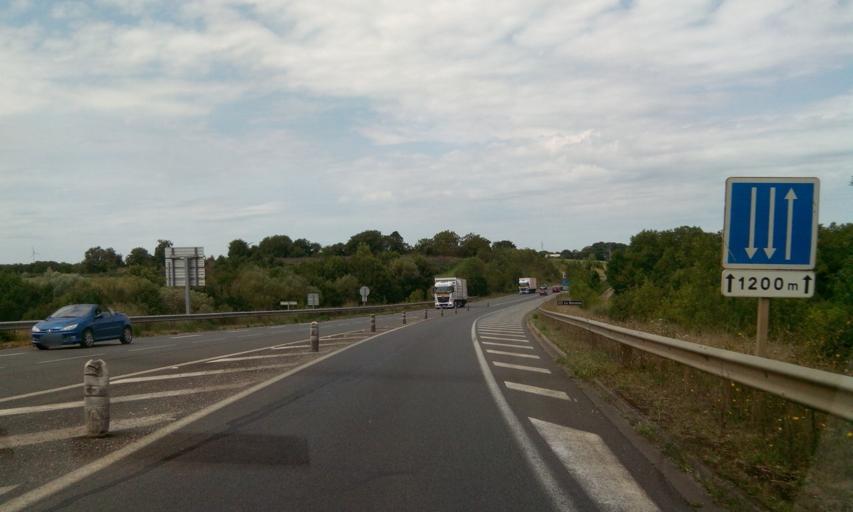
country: FR
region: Poitou-Charentes
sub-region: Departement des Deux-Sevres
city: Melle
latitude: 46.2098
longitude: -0.1502
